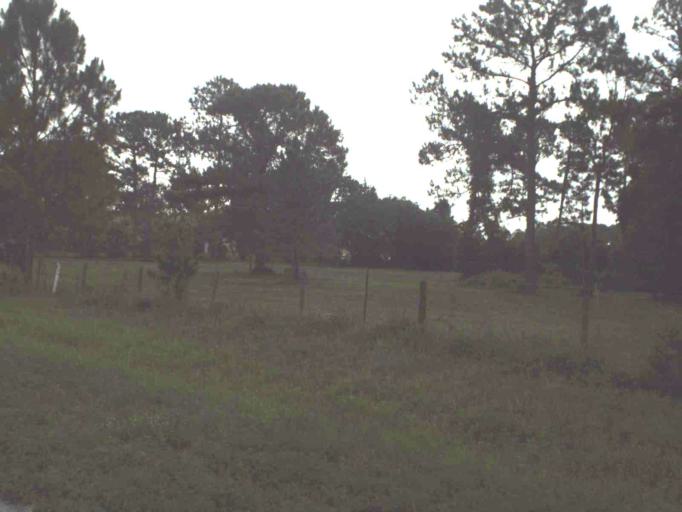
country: US
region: Florida
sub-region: Volusia County
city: Samsula-Spruce Creek
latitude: 28.9792
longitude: -81.0766
